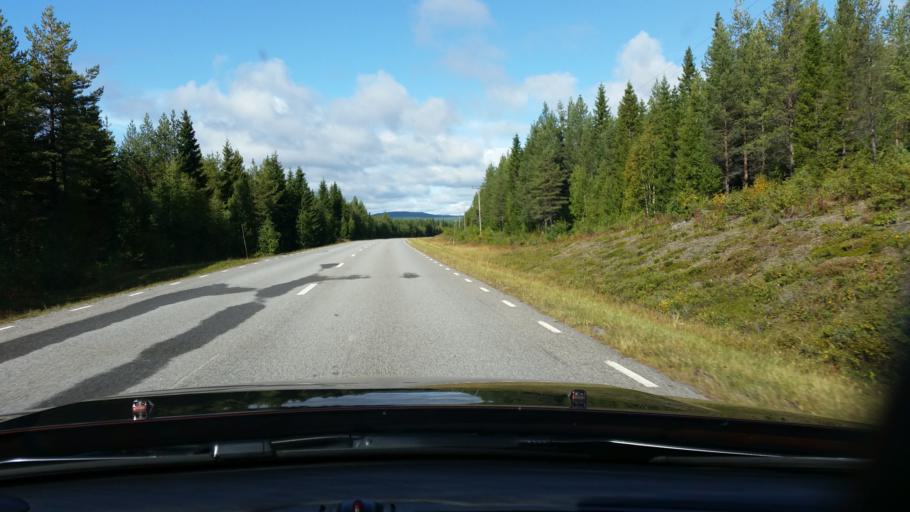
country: SE
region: Jaemtland
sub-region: Stroemsunds Kommun
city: Stroemsund
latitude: 64.2814
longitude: 15.3611
